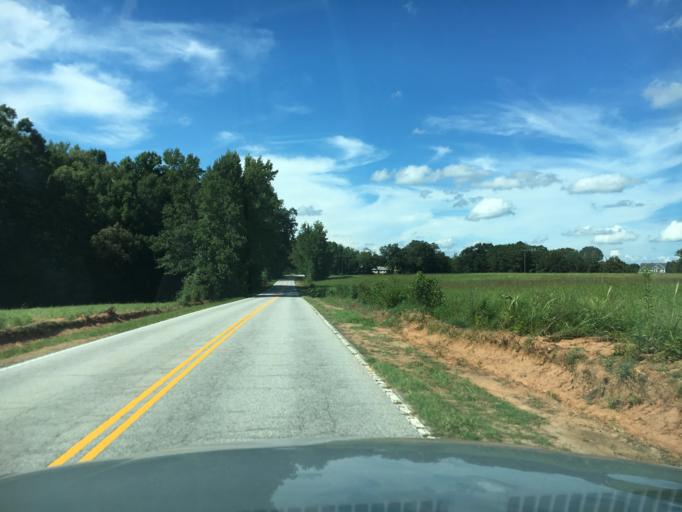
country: US
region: South Carolina
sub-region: Greenwood County
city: Ware Shoals
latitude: 34.4391
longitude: -82.2131
